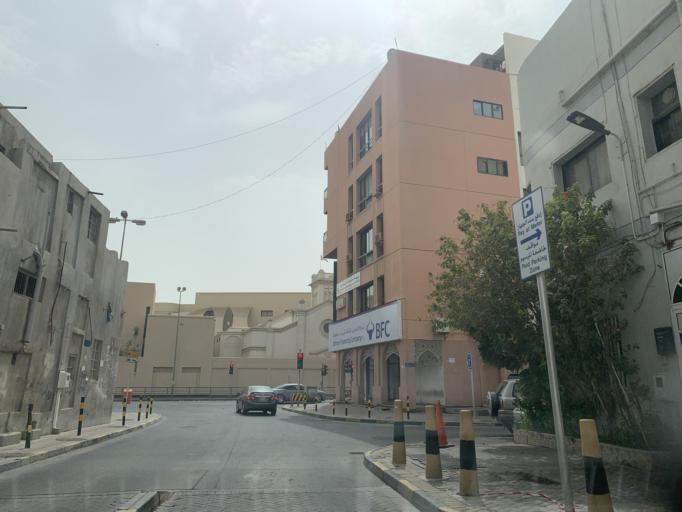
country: BH
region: Manama
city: Manama
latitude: 26.2278
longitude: 50.5790
